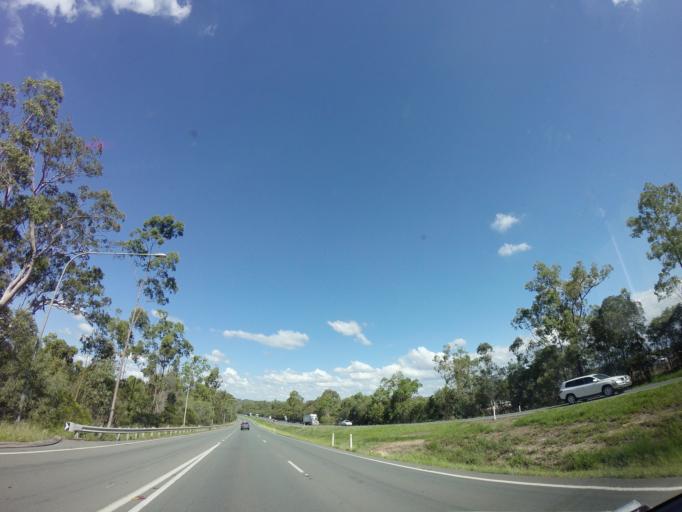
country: AU
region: Queensland
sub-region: Ipswich
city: Brassall
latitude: -27.5804
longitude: 152.7281
